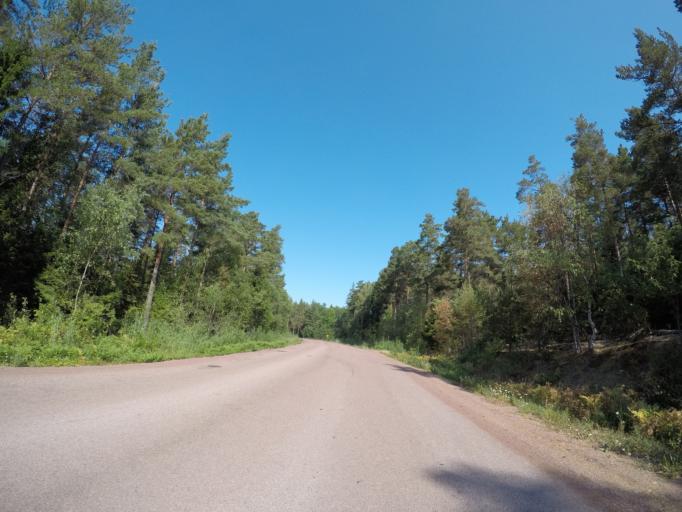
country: AX
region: Alands landsbygd
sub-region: Saltvik
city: Saltvik
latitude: 60.2313
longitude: 20.0064
